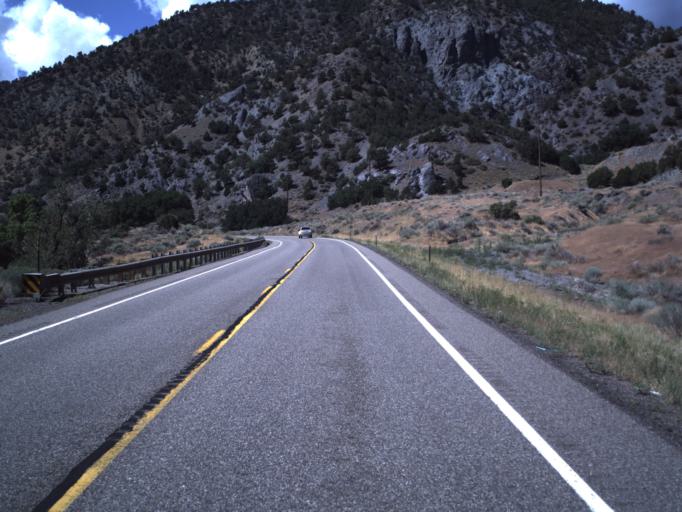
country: US
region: Utah
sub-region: Sevier County
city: Monroe
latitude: 38.5356
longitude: -112.2690
